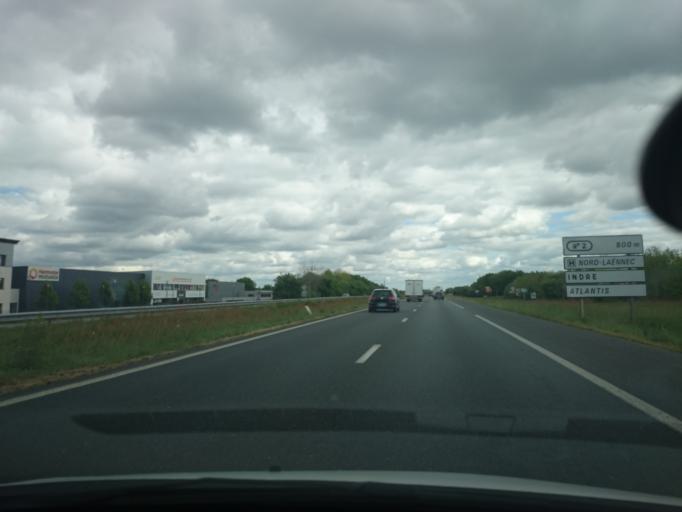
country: FR
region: Pays de la Loire
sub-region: Departement de la Loire-Atlantique
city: Saint-Herblain
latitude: 47.2370
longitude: -1.6586
